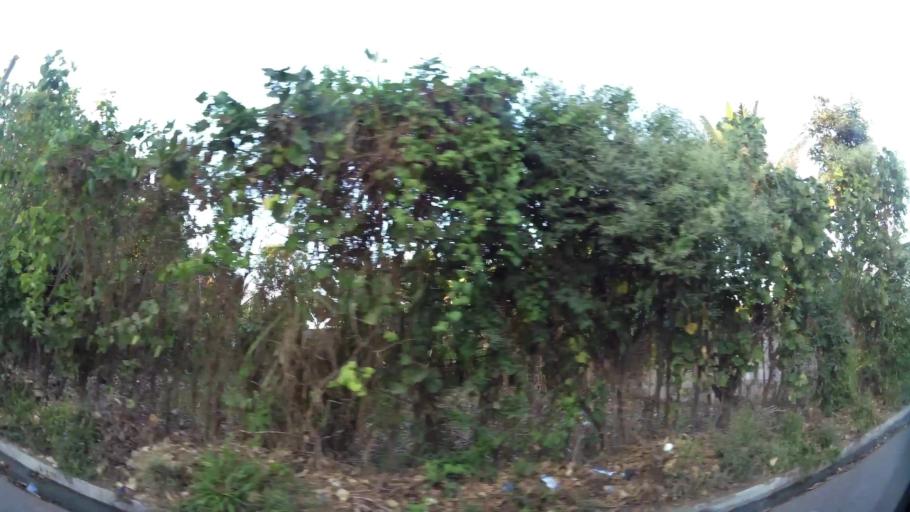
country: SV
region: Sonsonate
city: Armenia
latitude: 13.7385
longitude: -89.3874
